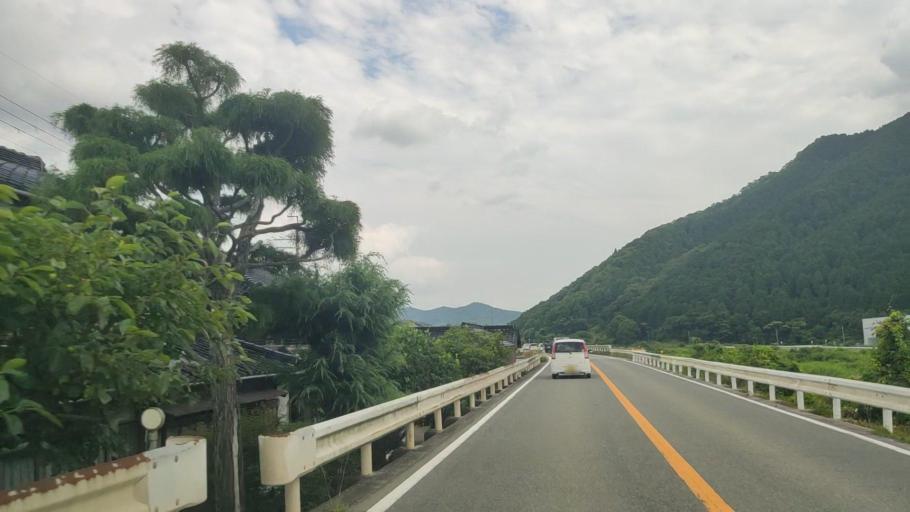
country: JP
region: Hyogo
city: Tatsunocho-tominaga
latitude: 34.9250
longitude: 134.5313
